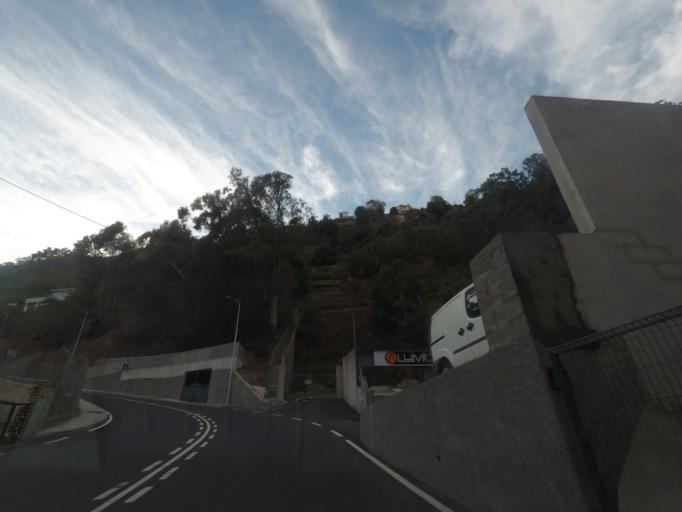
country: PT
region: Madeira
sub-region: Funchal
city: Nossa Senhora do Monte
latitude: 32.6799
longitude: -16.9352
